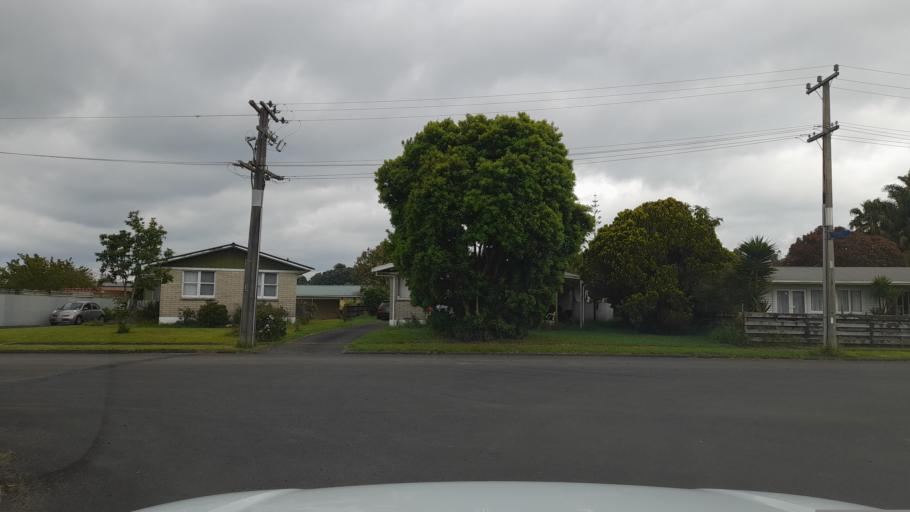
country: NZ
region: Northland
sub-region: Far North District
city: Waimate North
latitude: -35.4029
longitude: 173.7906
